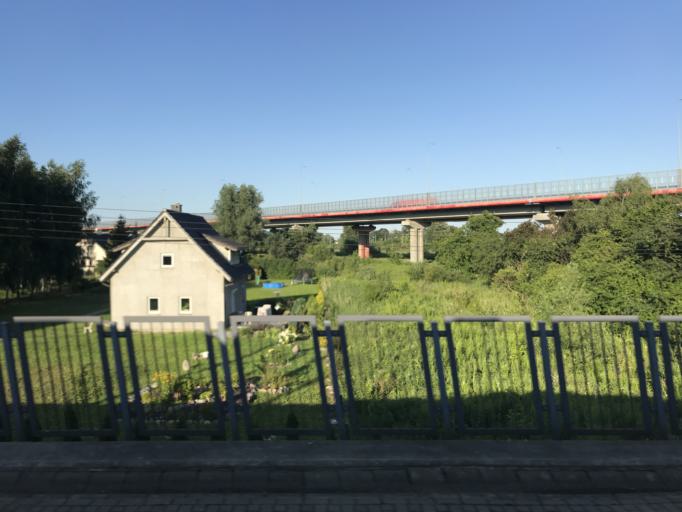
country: PL
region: Pomeranian Voivodeship
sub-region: Powiat gdanski
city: Pruszcz Gdanski
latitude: 54.3010
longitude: 18.6362
